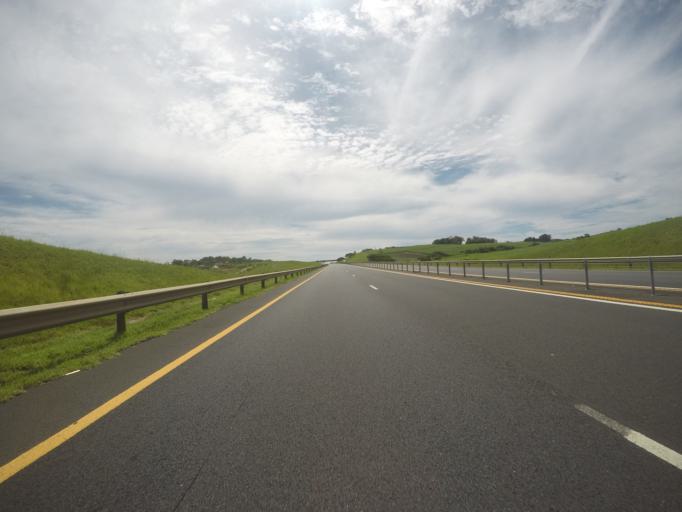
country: ZA
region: KwaZulu-Natal
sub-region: iLembe District Municipality
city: Mandeni
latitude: -29.1784
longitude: 31.5020
